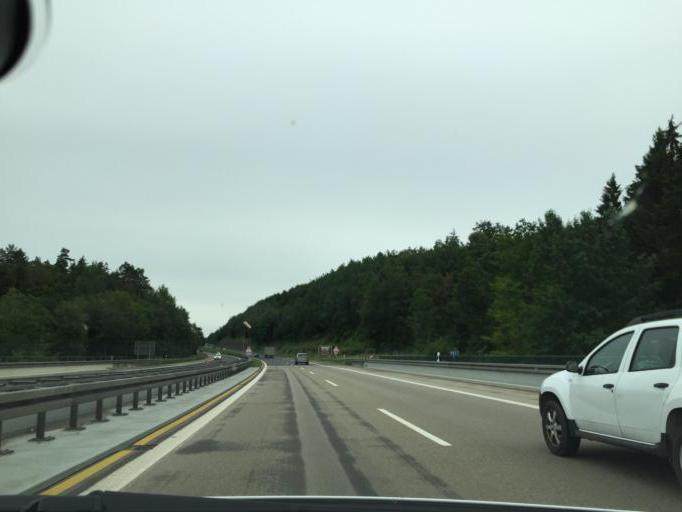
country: DE
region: Bavaria
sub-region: Regierungsbezirk Unterfranken
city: Motten
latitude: 50.3504
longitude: 9.7439
